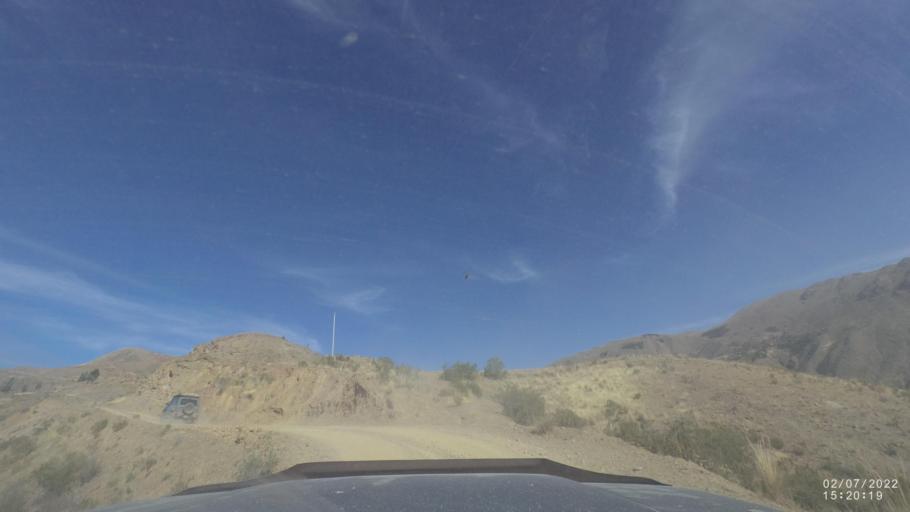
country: BO
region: Cochabamba
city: Irpa Irpa
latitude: -17.8686
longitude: -66.4276
